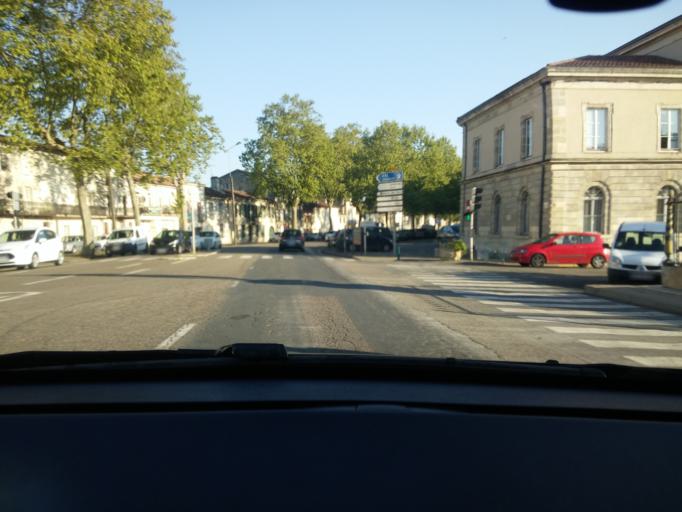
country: FR
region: Aquitaine
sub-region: Departement du Lot-et-Garonne
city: Nerac
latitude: 44.1354
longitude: 0.3368
